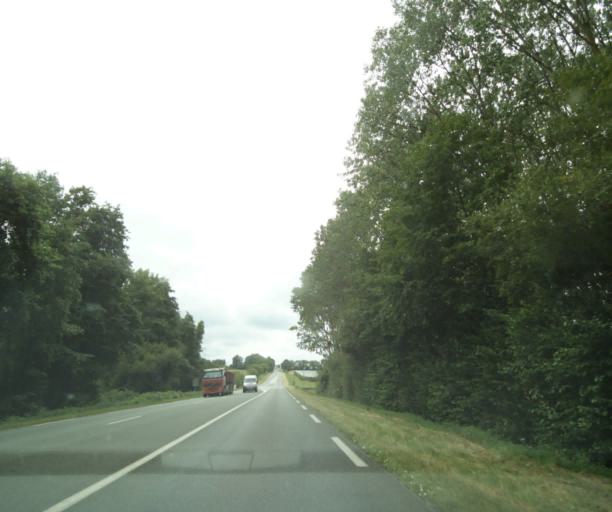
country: FR
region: Pays de la Loire
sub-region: Departement de Maine-et-Loire
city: Seiches-sur-le-Loir
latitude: 47.6198
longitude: -0.3170
